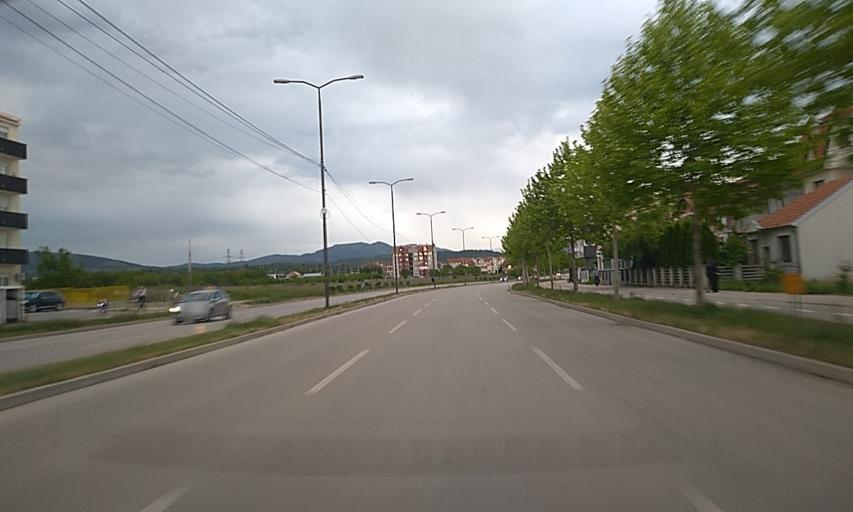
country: RS
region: Central Serbia
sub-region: Nisavski Okrug
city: Nis
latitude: 43.3360
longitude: 21.9315
